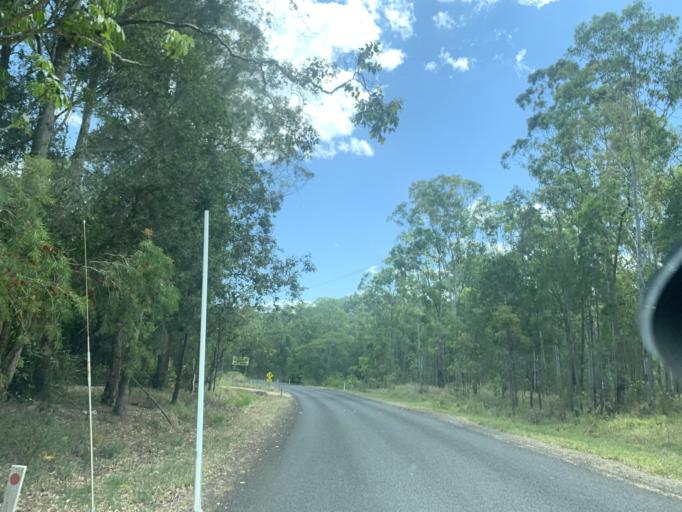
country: AU
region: Queensland
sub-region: Tablelands
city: Atherton
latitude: -17.3206
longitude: 145.4411
